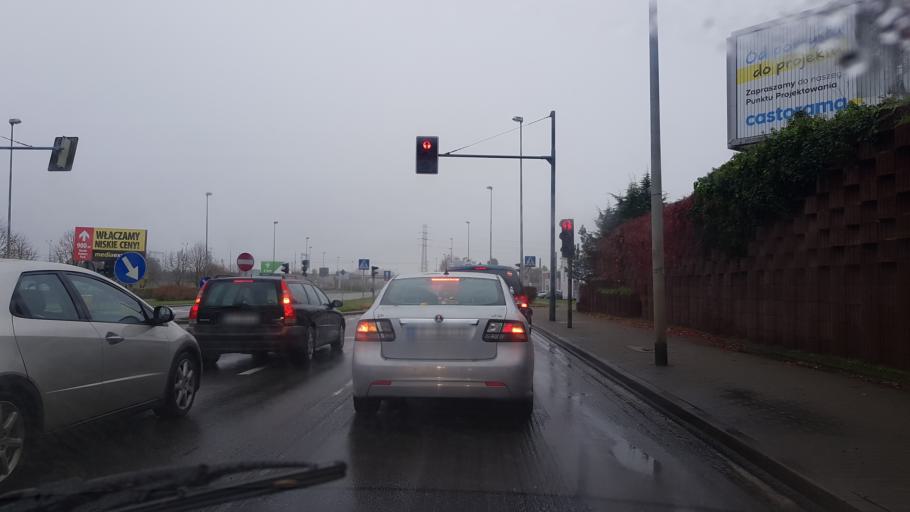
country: PL
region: West Pomeranian Voivodeship
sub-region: Powiat policki
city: Przeclaw
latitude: 53.4010
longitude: 14.5011
